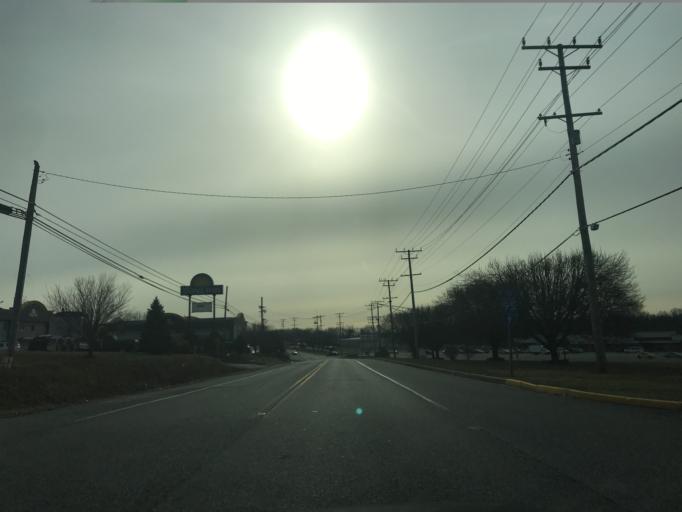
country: US
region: Maryland
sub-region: Harford County
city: Aberdeen
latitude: 39.5225
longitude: -76.1886
